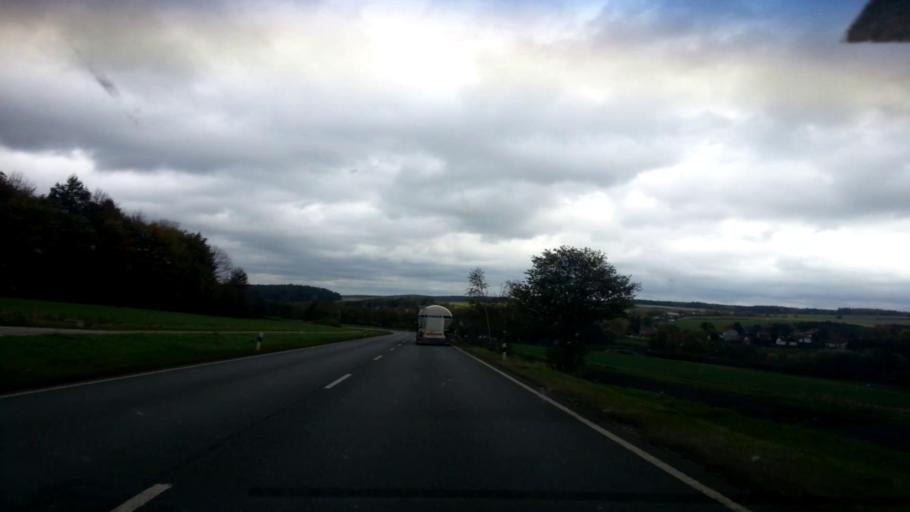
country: DE
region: Bavaria
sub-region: Upper Franconia
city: Bad Alexandersbad
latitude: 50.0226
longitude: 12.0094
